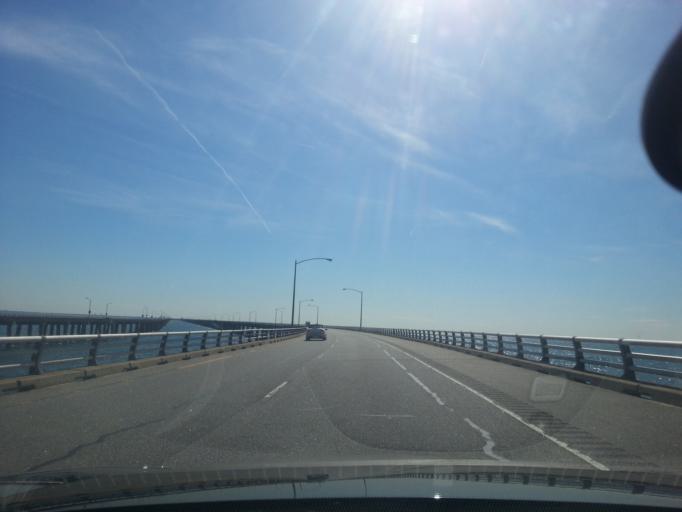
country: US
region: Virginia
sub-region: City of Virginia Beach
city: Virginia Beach
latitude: 37.0306
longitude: -76.0862
